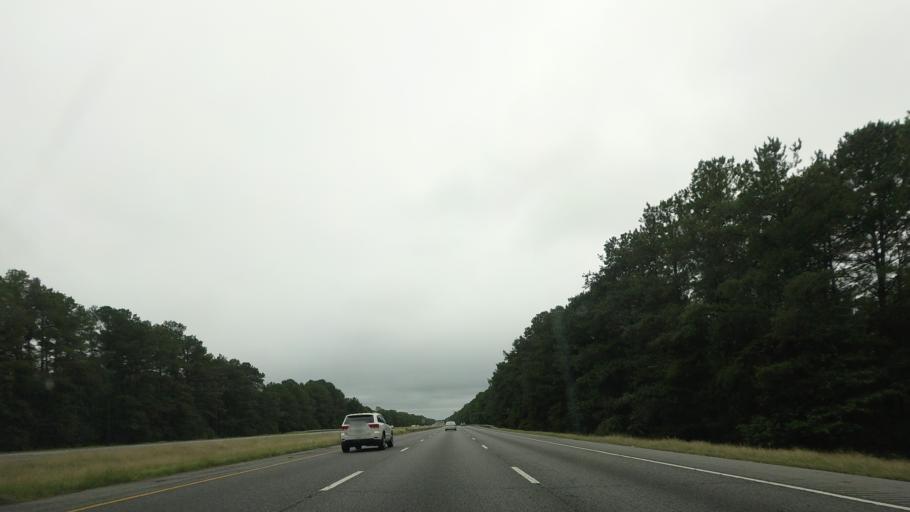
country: US
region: Georgia
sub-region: Houston County
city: Perry
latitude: 32.3802
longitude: -83.7683
